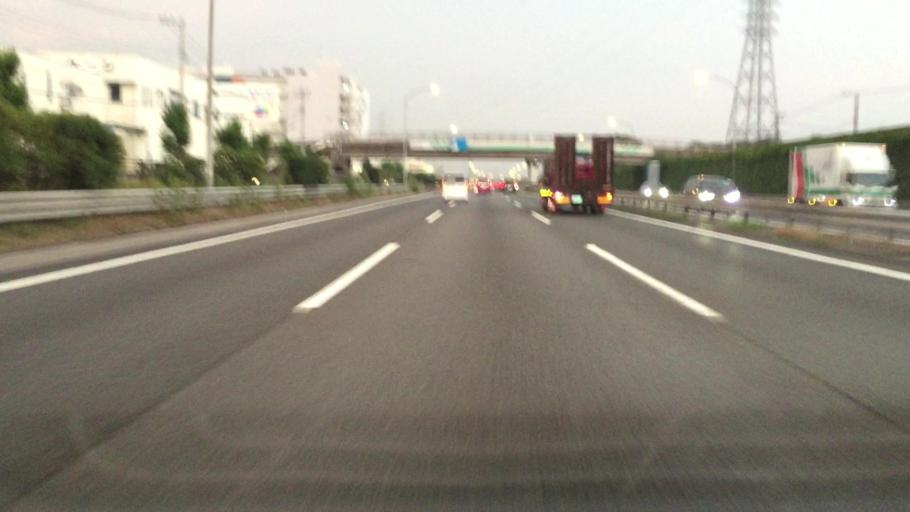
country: JP
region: Saitama
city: Iwatsuki
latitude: 35.9325
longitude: 139.6958
